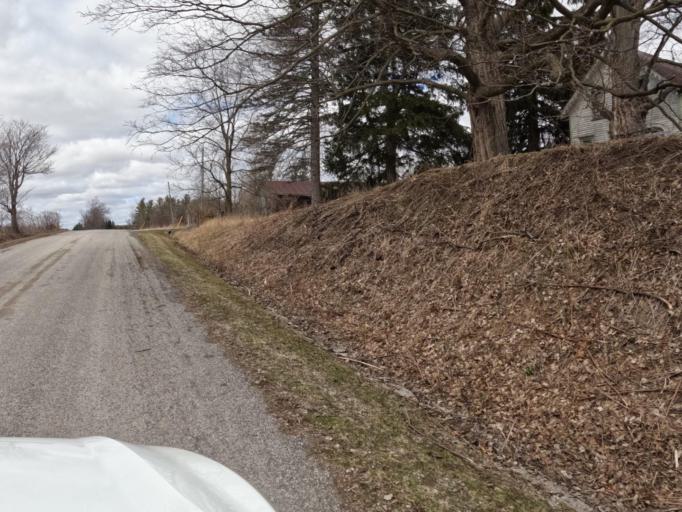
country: CA
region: Ontario
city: Norfolk County
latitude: 42.8385
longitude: -80.1667
